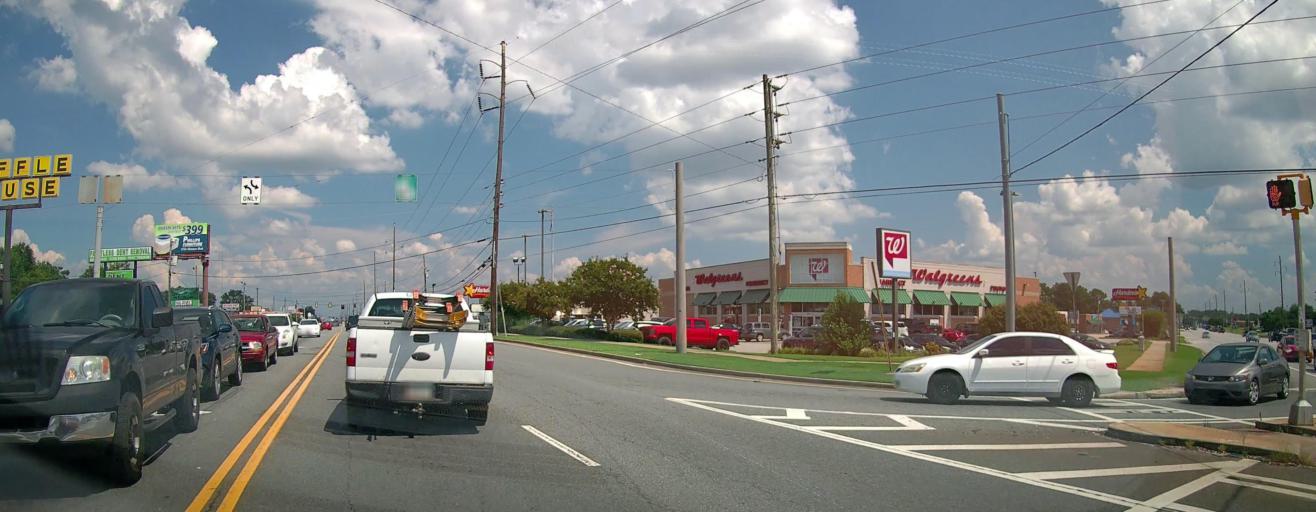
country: US
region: Georgia
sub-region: Houston County
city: Centerville
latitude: 32.6133
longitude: -83.6880
